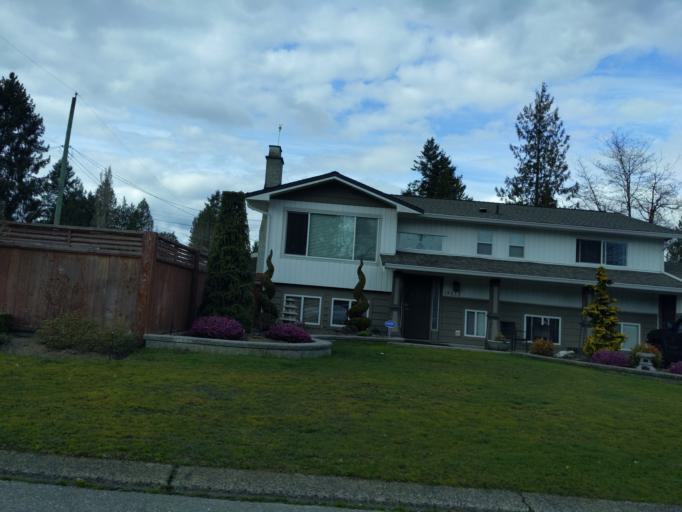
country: CA
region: British Columbia
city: Pitt Meadows
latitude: 49.2153
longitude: -122.6802
